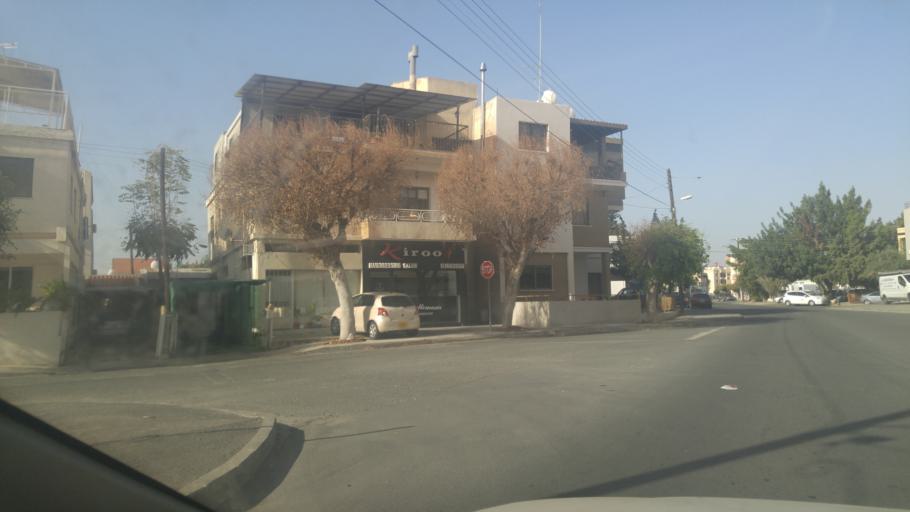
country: CY
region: Limassol
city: Limassol
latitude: 34.6820
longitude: 33.0223
